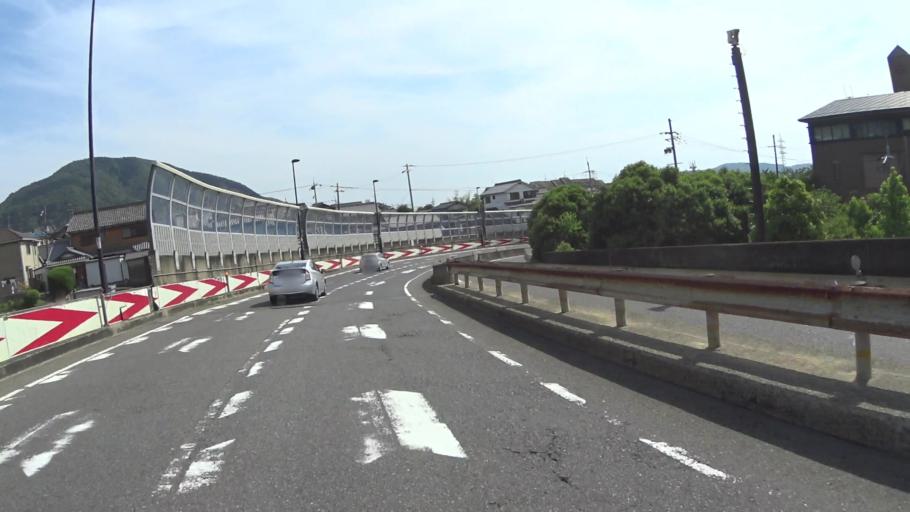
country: JP
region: Shiga Prefecture
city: Otsu-shi
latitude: 34.9921
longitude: 135.8346
